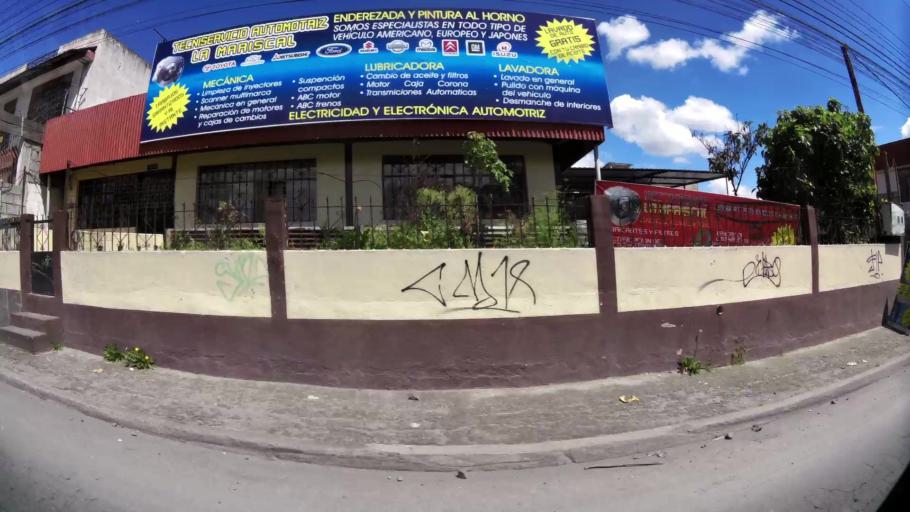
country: EC
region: Pichincha
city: Quito
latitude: -0.3138
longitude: -78.5584
